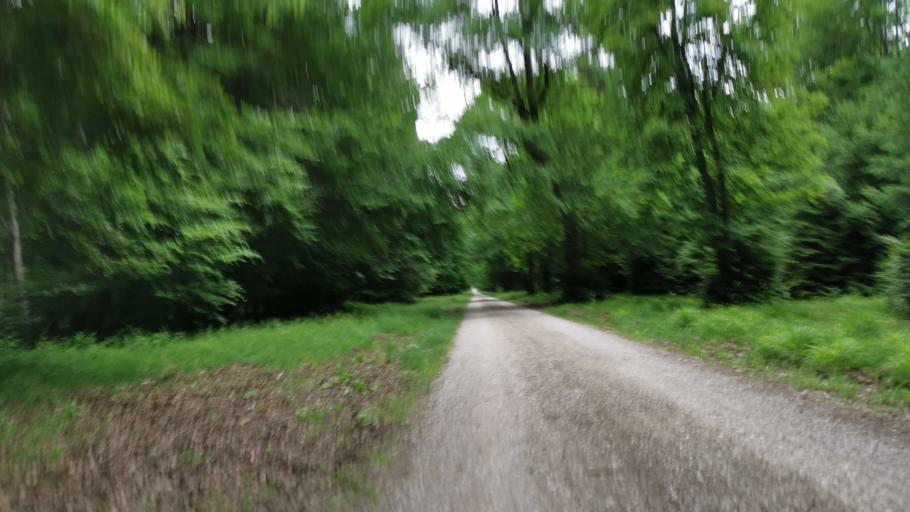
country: DE
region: Bavaria
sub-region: Upper Bavaria
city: Baierbrunn
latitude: 48.0311
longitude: 11.4548
